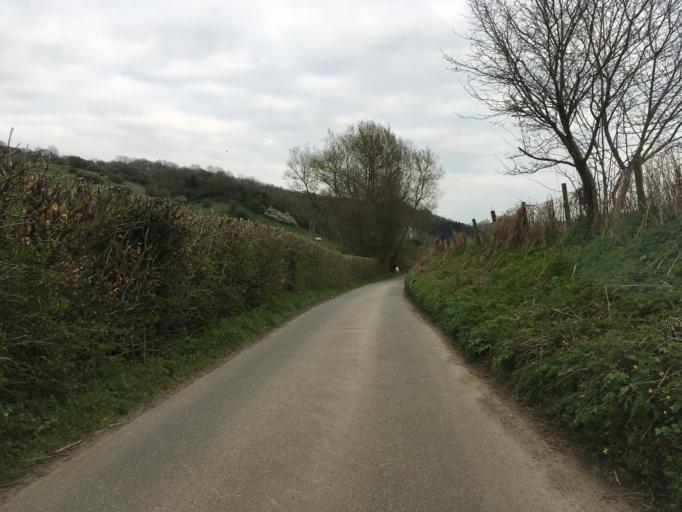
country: GB
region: England
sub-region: Gloucestershire
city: Wotton-under-Edge
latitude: 51.6047
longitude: -2.3154
